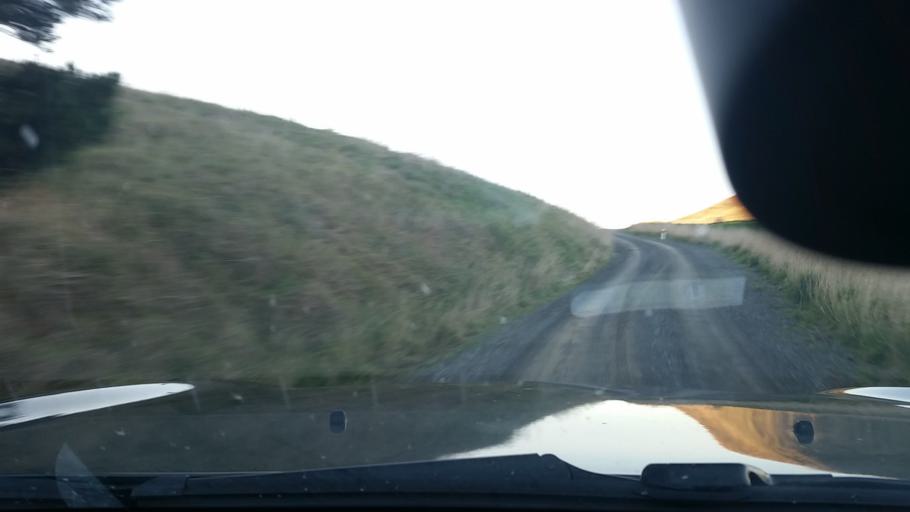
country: NZ
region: Marlborough
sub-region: Marlborough District
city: Blenheim
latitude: -41.7409
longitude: 174.0489
